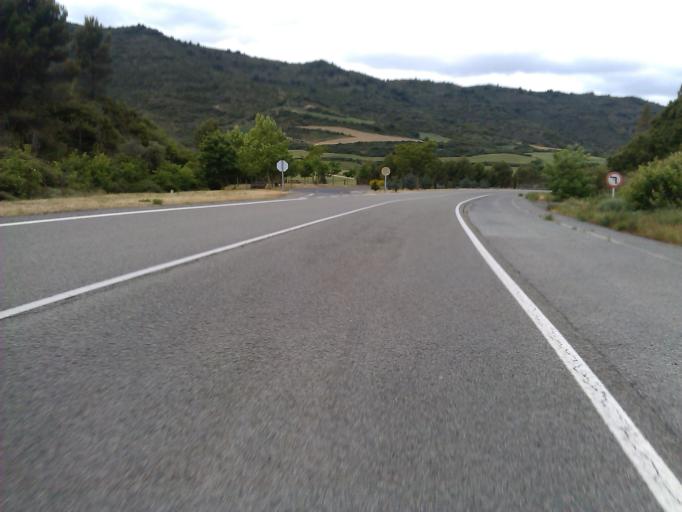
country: ES
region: Navarre
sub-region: Provincia de Navarra
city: Cirauqui
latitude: 42.6732
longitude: -1.9081
